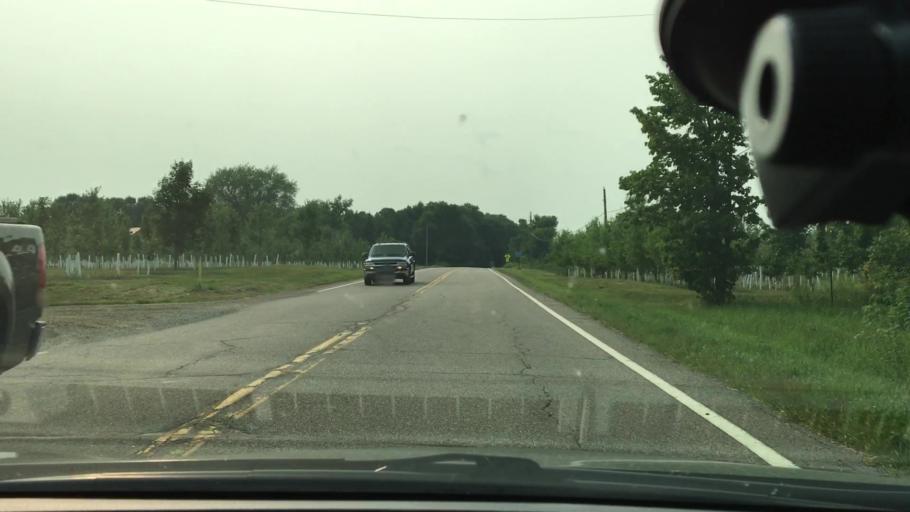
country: US
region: Minnesota
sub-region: Hennepin County
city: Dayton
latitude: 45.2234
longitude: -93.4827
